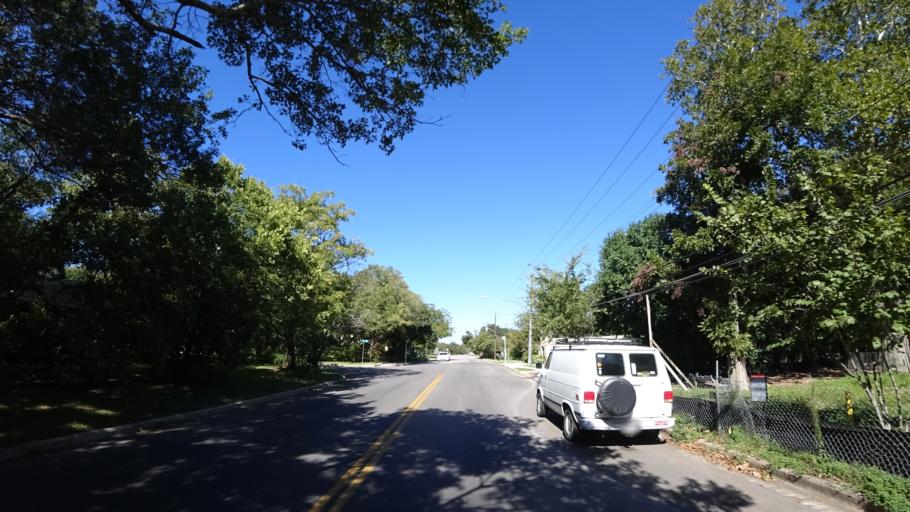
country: US
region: Texas
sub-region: Travis County
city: West Lake Hills
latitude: 30.3228
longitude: -97.7521
